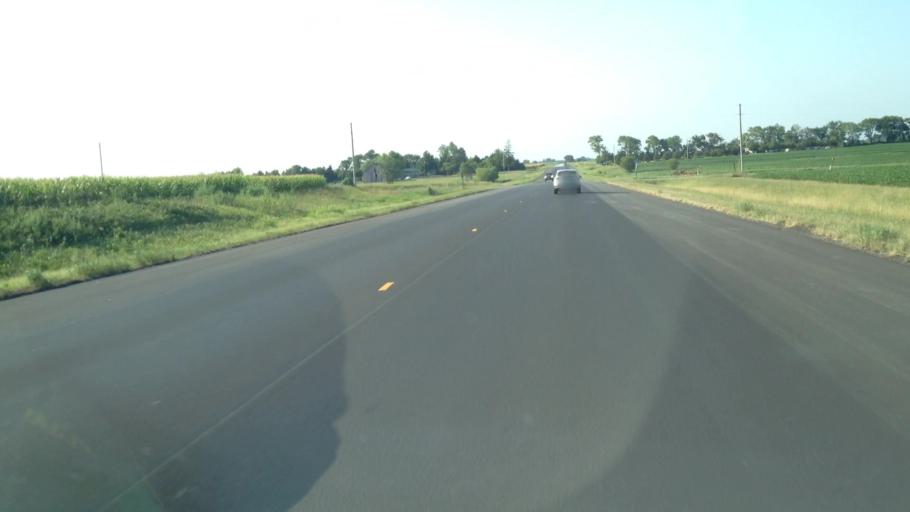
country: US
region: Kansas
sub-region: Anderson County
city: Garnett
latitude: 38.4469
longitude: -95.2488
